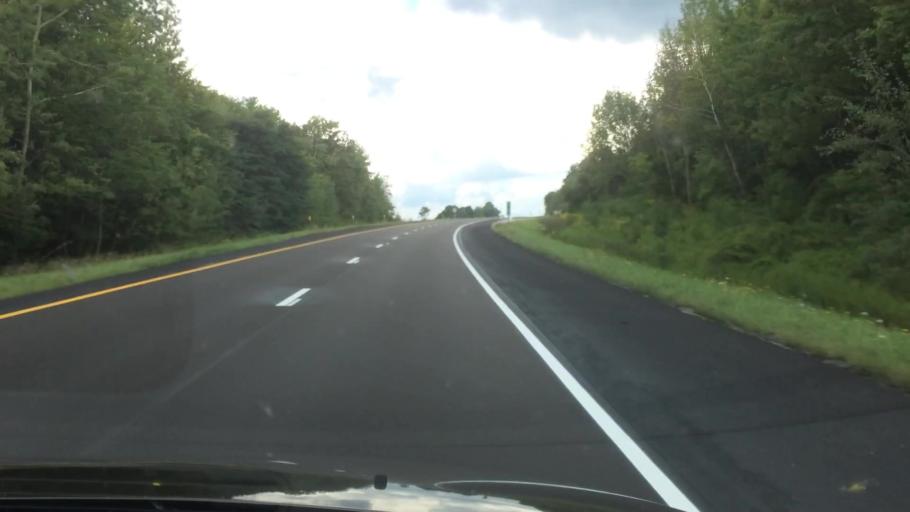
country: US
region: New York
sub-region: Chautauqua County
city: Lakewood
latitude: 42.1390
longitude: -79.3480
